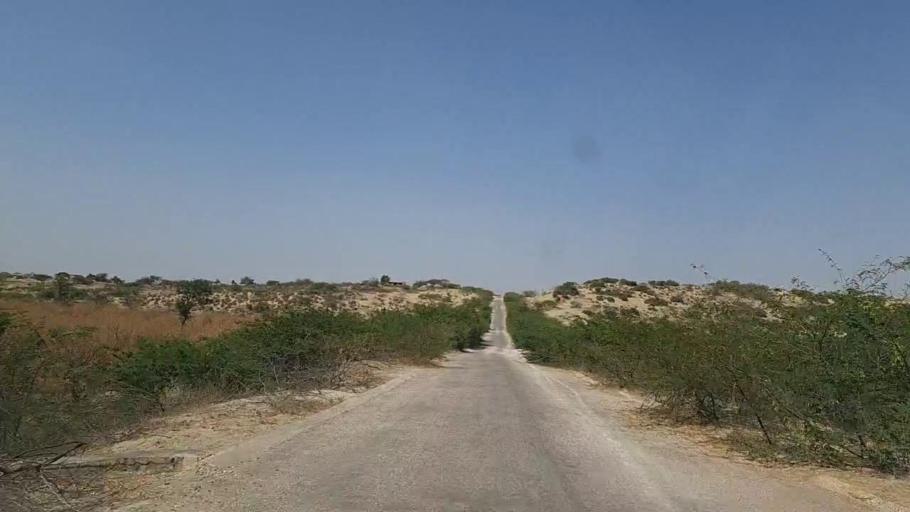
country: PK
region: Sindh
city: Naukot
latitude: 24.5861
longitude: 69.3179
